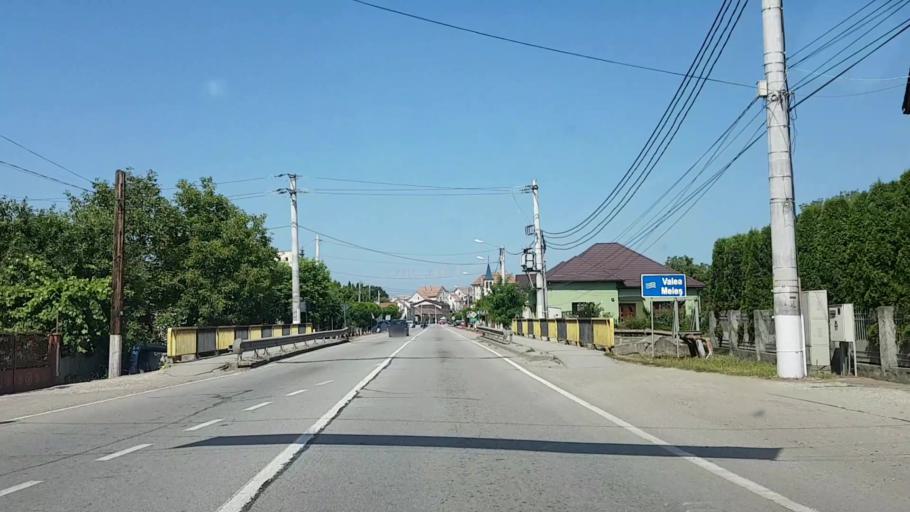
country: RO
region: Bistrita-Nasaud
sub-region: Comuna Beclean
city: Beclean
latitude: 47.1759
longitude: 24.1706
